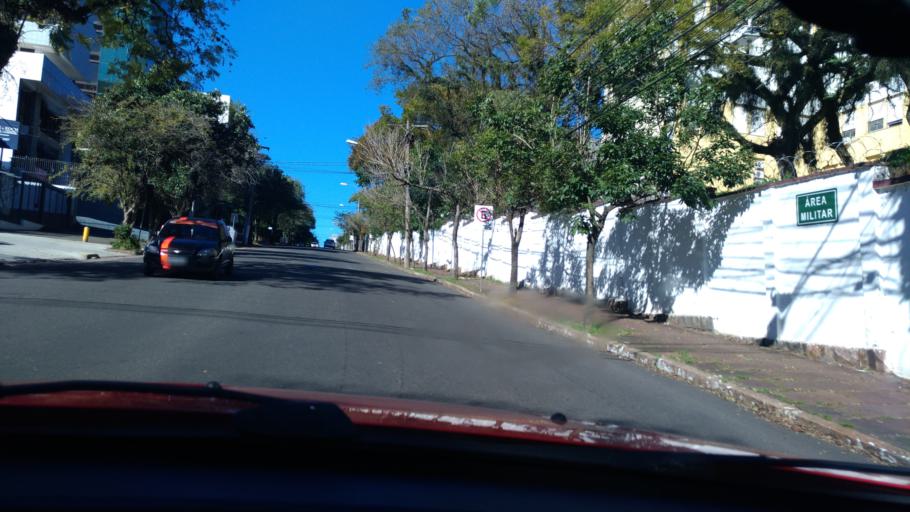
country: BR
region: Rio Grande do Sul
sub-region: Porto Alegre
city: Porto Alegre
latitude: -30.0178
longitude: -51.1931
